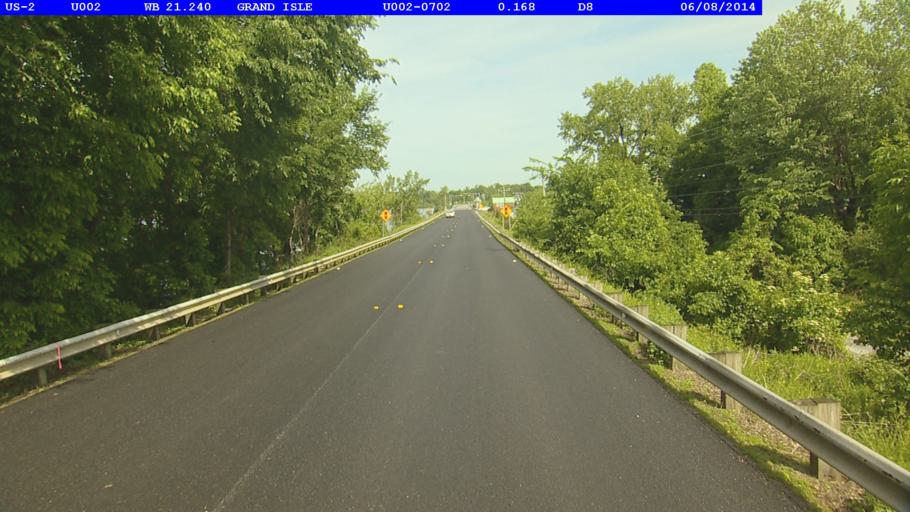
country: US
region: Vermont
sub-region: Grand Isle County
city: North Hero
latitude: 44.7643
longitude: -73.2877
